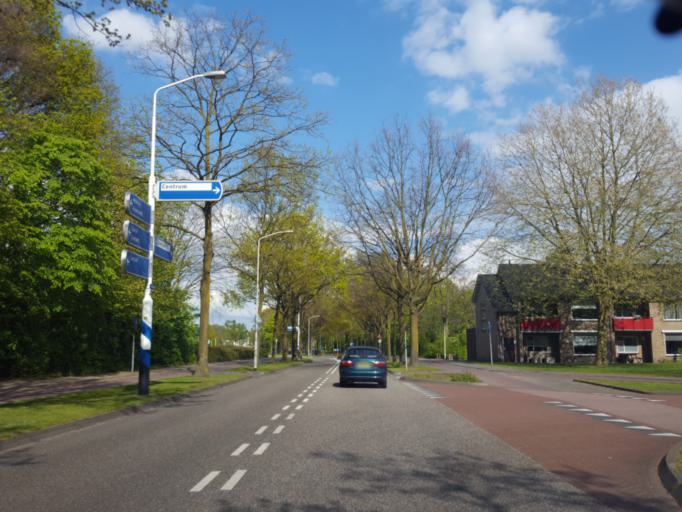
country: NL
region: North Brabant
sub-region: Gemeente Asten
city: Asten
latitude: 51.4672
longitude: 5.7903
